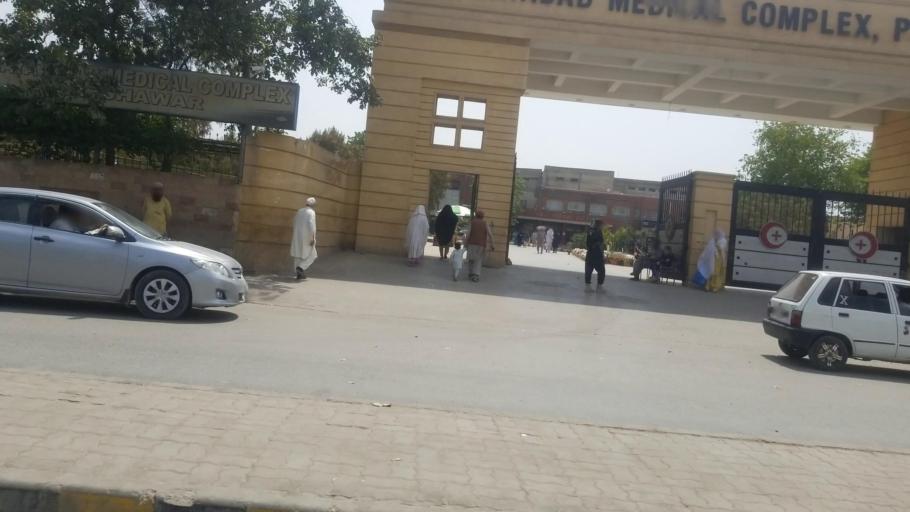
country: PK
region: Khyber Pakhtunkhwa
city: Peshawar
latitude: 33.9939
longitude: 71.4501
